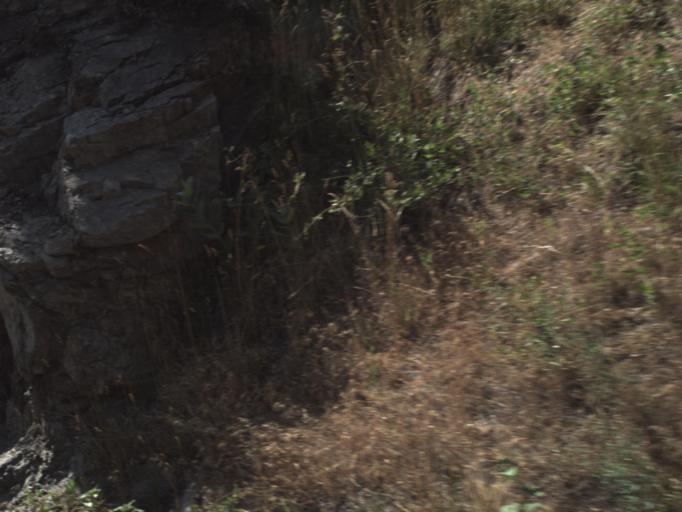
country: US
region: Utah
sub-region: Weber County
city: Liberty
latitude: 41.2546
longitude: -111.8612
